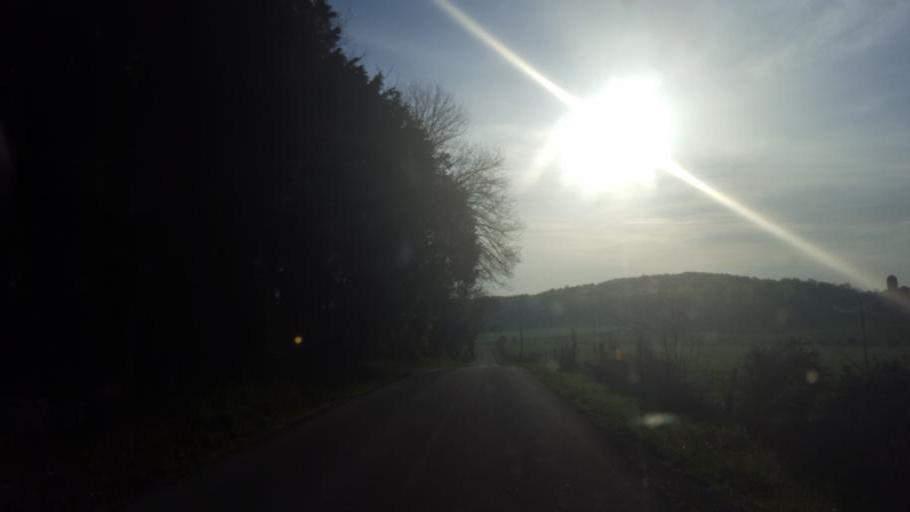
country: US
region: Kentucky
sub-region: Hart County
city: Munfordville
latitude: 37.2450
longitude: -85.9143
